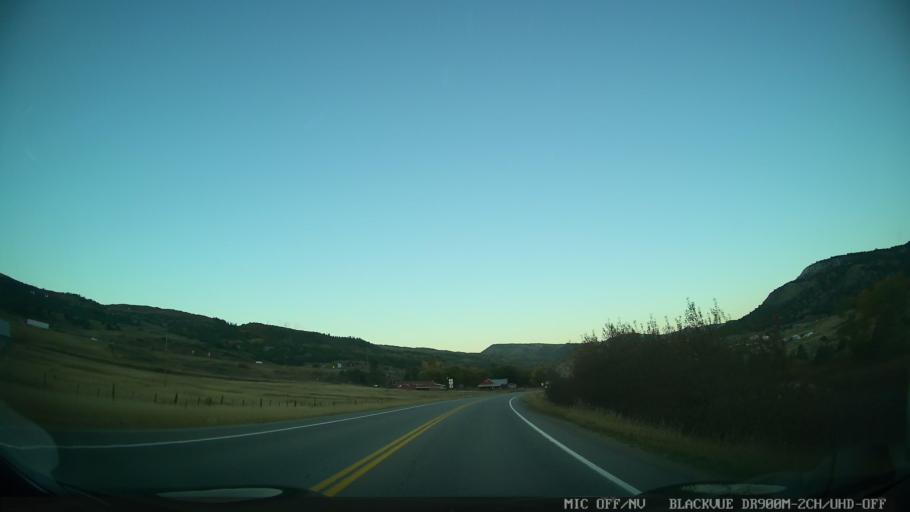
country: US
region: Colorado
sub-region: Eagle County
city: Edwards
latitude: 39.7005
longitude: -106.6721
